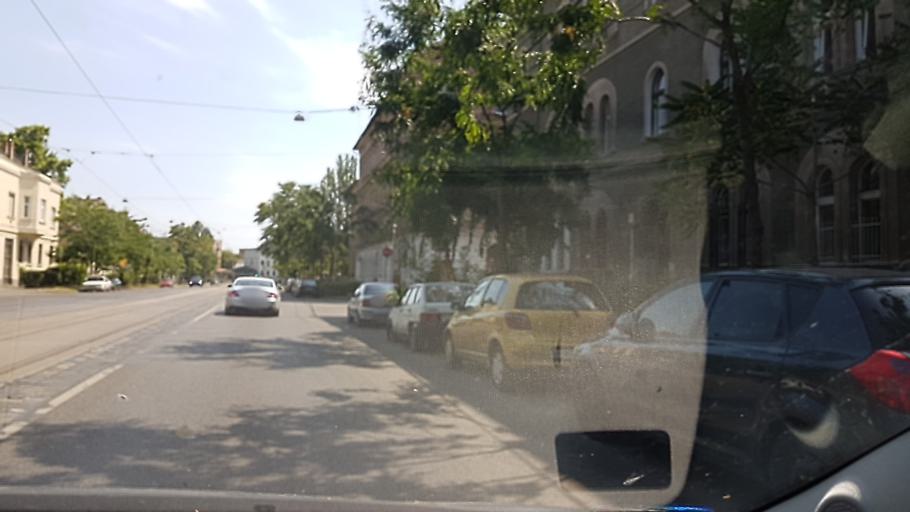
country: HU
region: Budapest
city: Budapest VIII. keruelet
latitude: 47.4835
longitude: 19.0931
